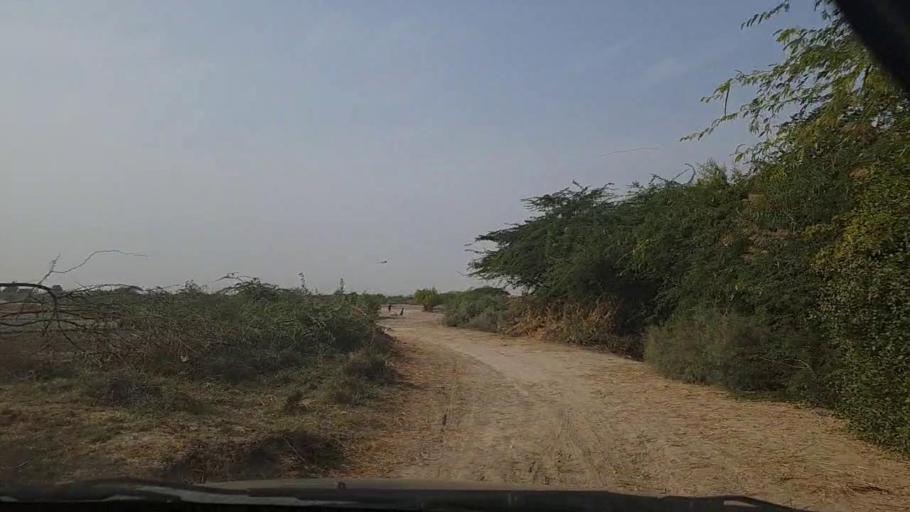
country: PK
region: Sindh
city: Thatta
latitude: 24.6133
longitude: 67.9538
